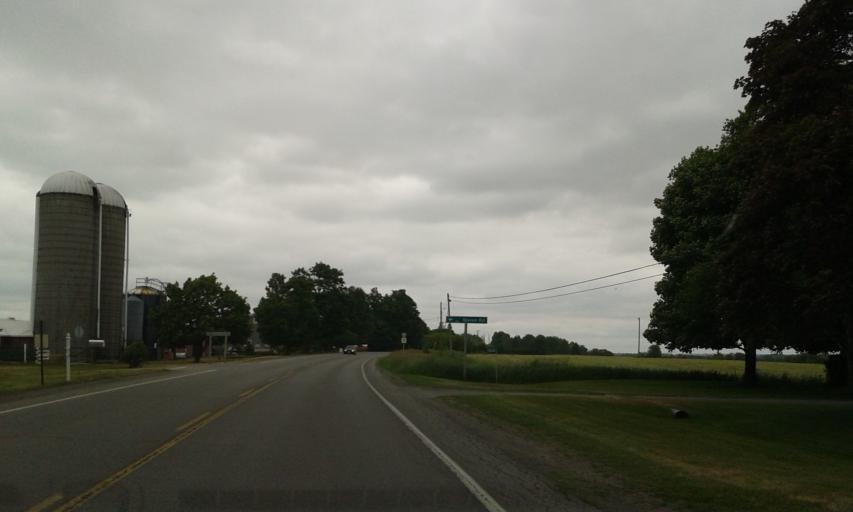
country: CA
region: Ontario
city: Prince Edward
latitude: 43.9711
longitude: -77.2763
